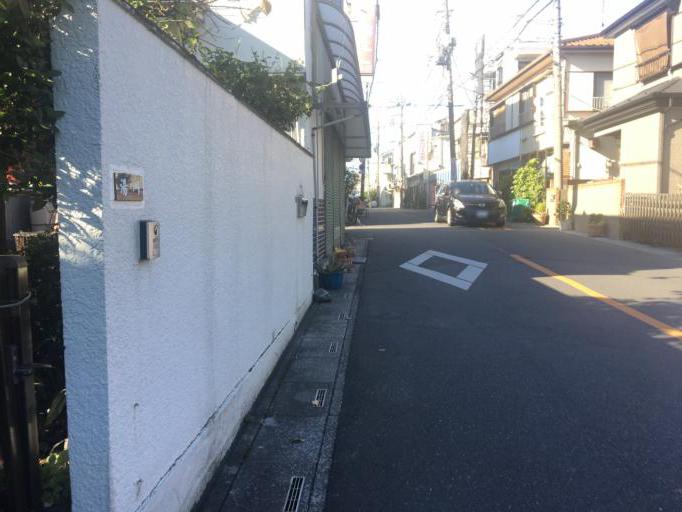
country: JP
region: Saitama
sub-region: Kawaguchi-shi
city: Hatogaya-honcho
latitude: 35.8327
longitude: 139.7421
